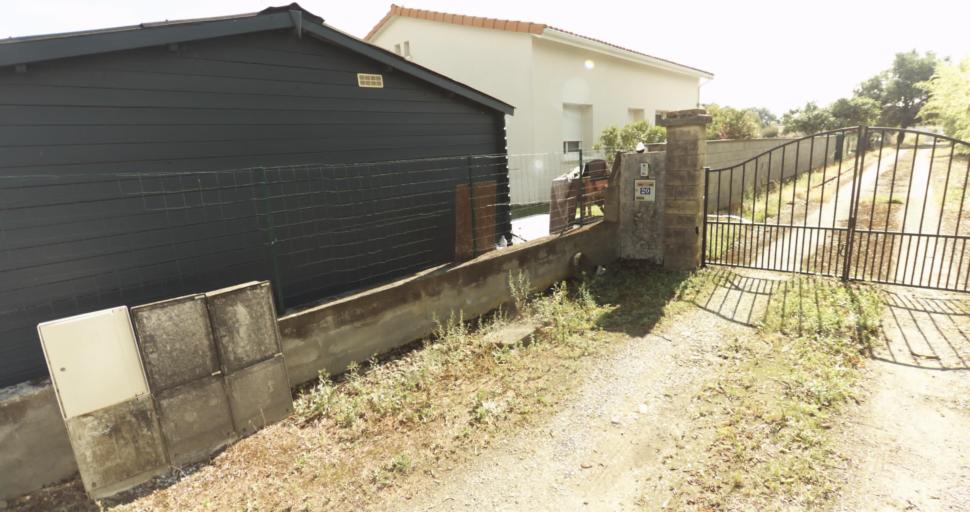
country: FR
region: Midi-Pyrenees
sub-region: Departement de la Haute-Garonne
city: Fontenilles
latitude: 43.5627
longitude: 1.2097
